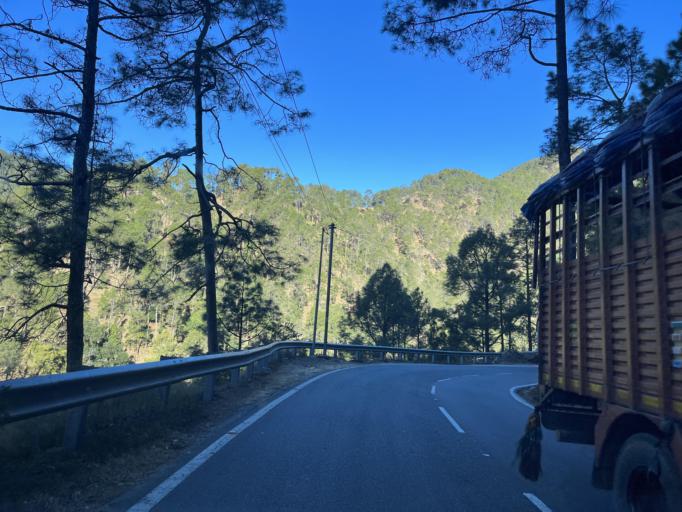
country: IN
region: Uttarakhand
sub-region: Naini Tal
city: Bhowali
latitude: 29.4030
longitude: 79.5103
